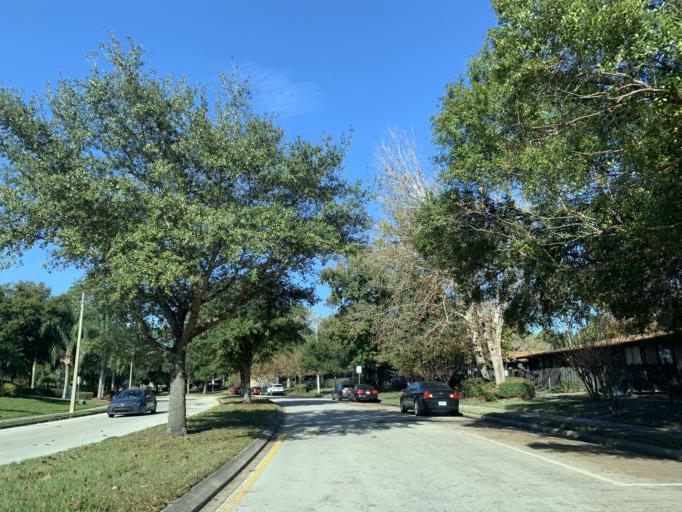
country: US
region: Florida
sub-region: Orange County
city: Oak Ridge
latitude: 28.4907
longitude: -81.4399
